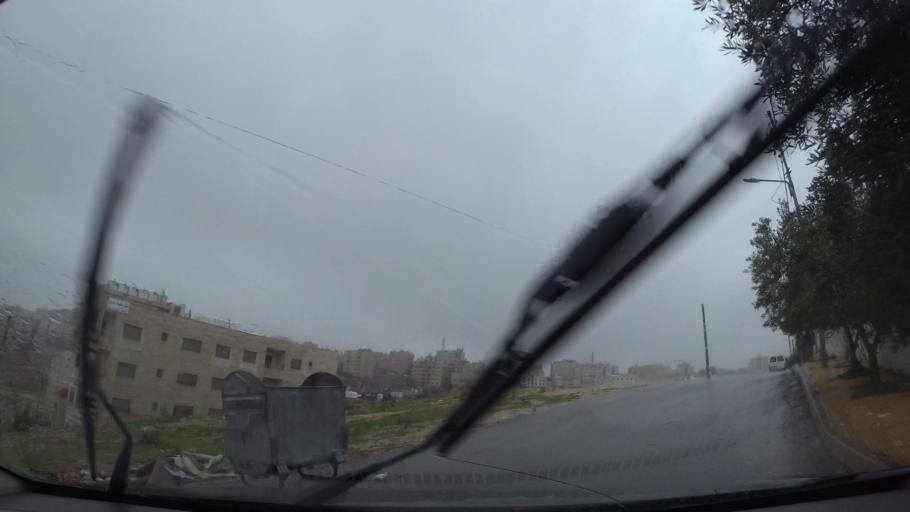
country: JO
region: Amman
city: Al Jubayhah
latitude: 32.0112
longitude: 35.8880
